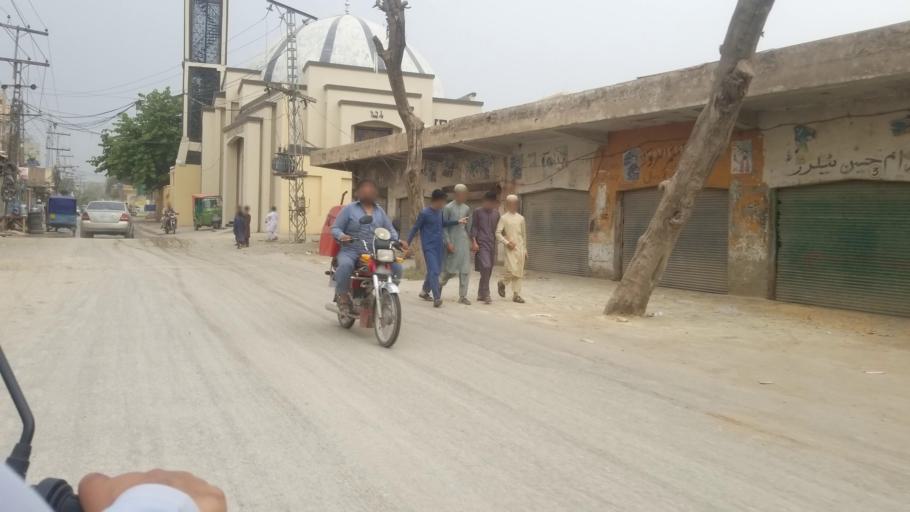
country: PK
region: Khyber Pakhtunkhwa
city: Peshawar
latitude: 33.9856
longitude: 71.5541
